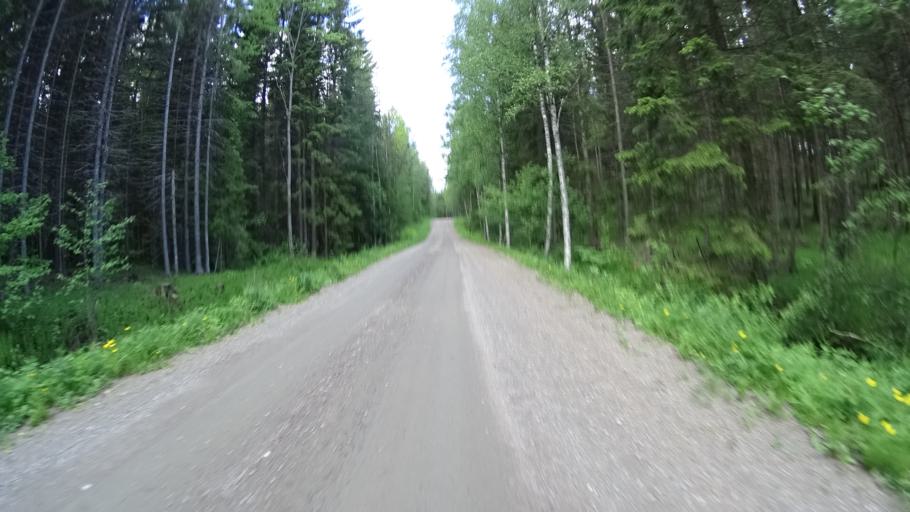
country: FI
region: Uusimaa
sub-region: Raaseporin
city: Pohja
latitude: 60.1636
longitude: 23.6049
